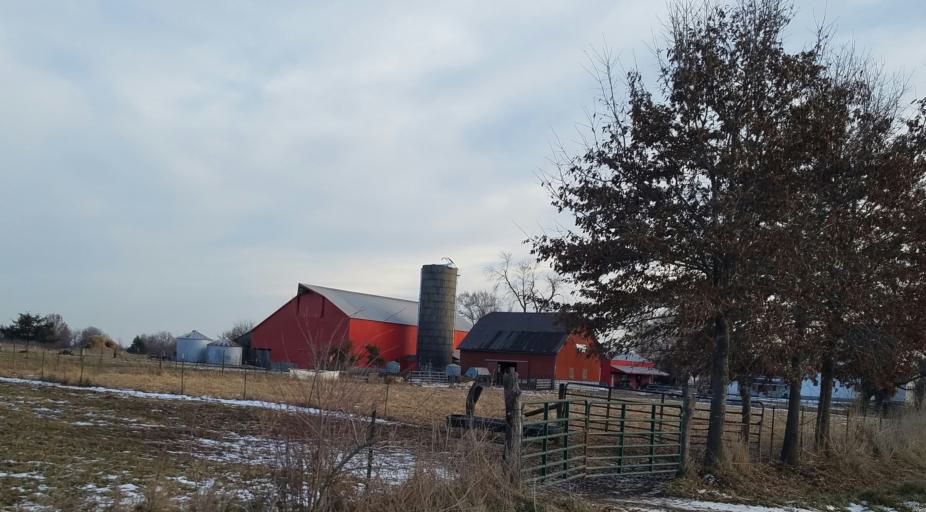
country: US
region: Missouri
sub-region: Randolph County
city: Moberly
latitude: 39.3413
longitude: -92.3107
